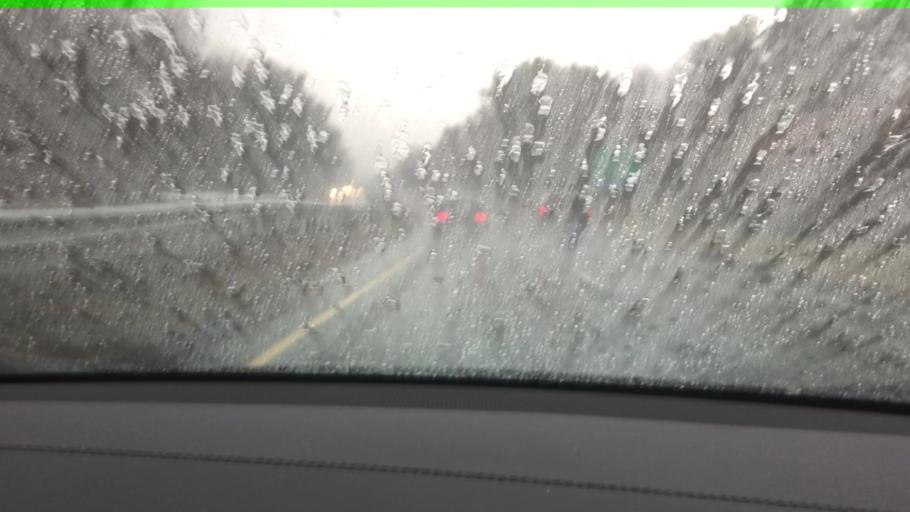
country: US
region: Connecticut
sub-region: New Haven County
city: Hamden
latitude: 41.3770
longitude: -72.9068
